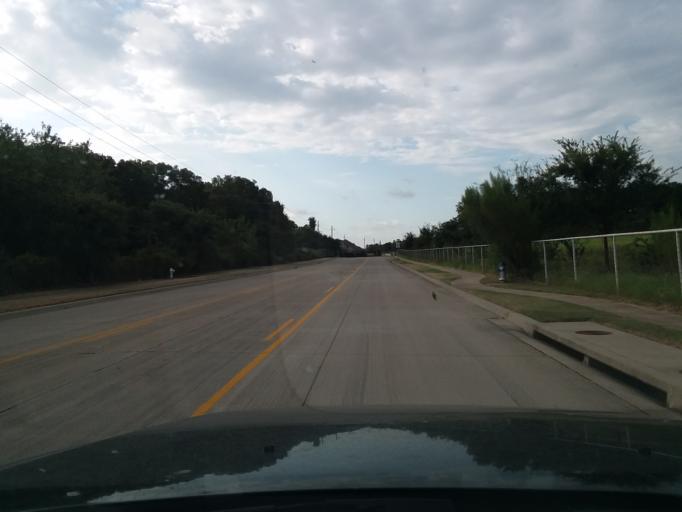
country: US
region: Texas
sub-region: Denton County
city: Hickory Creek
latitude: 33.1282
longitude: -97.0610
